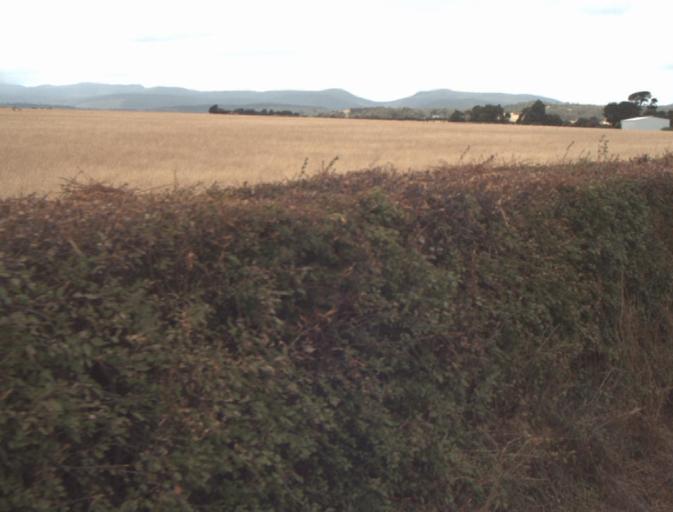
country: AU
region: Tasmania
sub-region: Northern Midlands
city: Evandale
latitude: -41.5252
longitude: 147.2675
